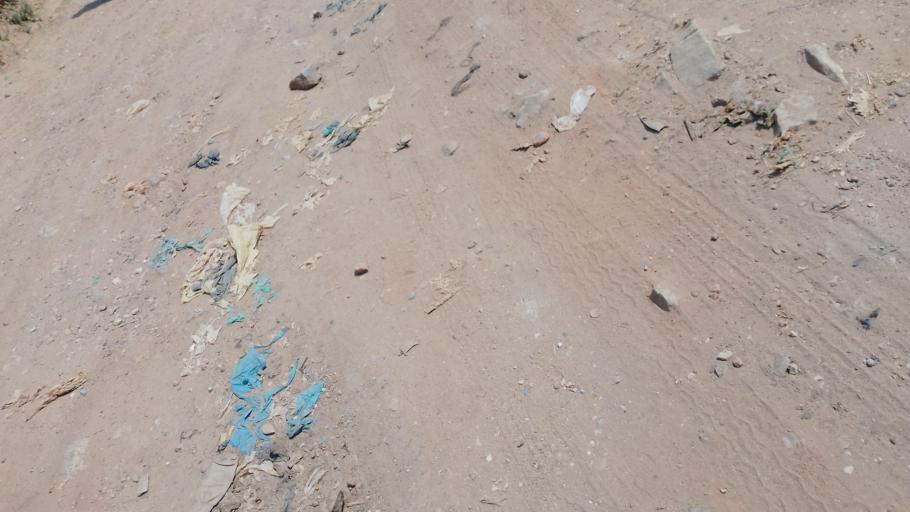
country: ZM
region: Lusaka
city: Lusaka
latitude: -15.3982
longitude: 28.3685
